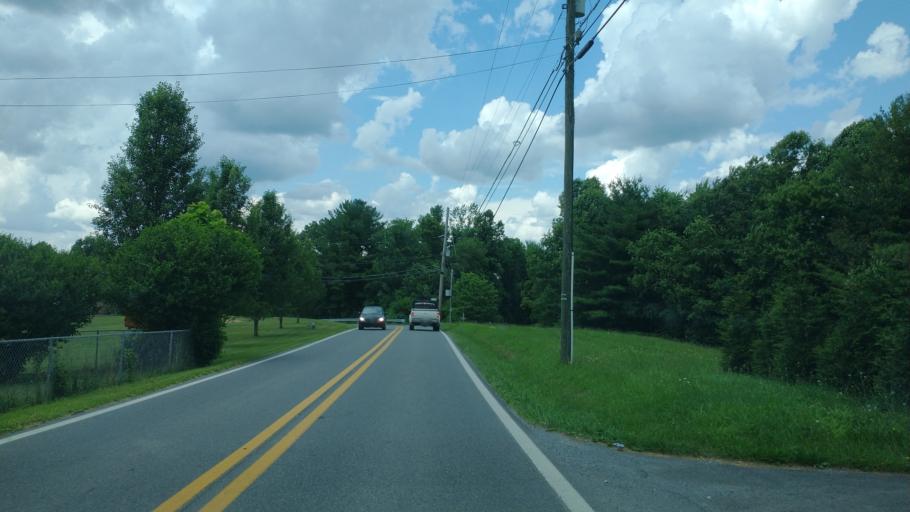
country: US
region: West Virginia
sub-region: Mercer County
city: Athens
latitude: 37.4149
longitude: -81.0609
